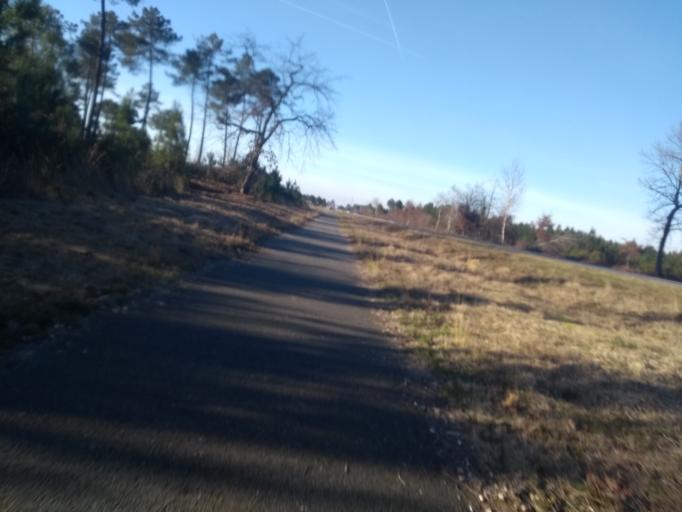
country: FR
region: Aquitaine
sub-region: Departement de la Gironde
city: Le Barp
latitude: 44.6184
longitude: -0.7818
